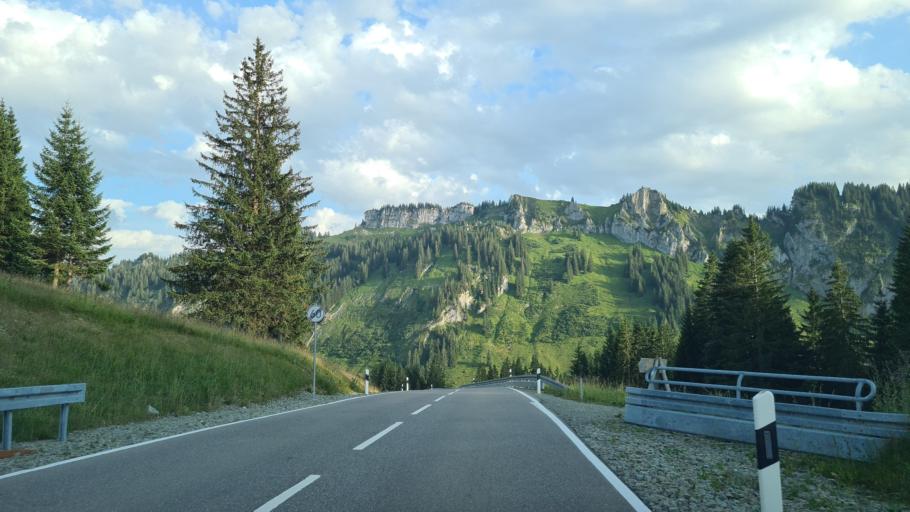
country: DE
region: Bavaria
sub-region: Swabia
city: Obermaiselstein
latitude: 47.4368
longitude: 10.1771
